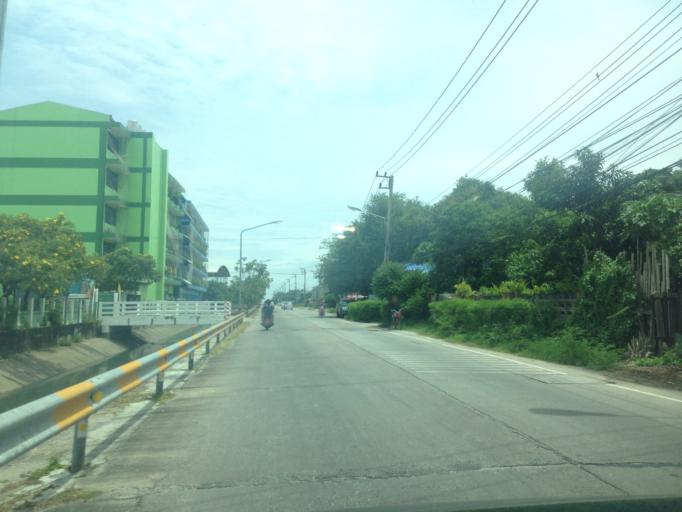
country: TH
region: Chon Buri
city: Chon Buri
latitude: 13.3747
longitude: 100.9858
